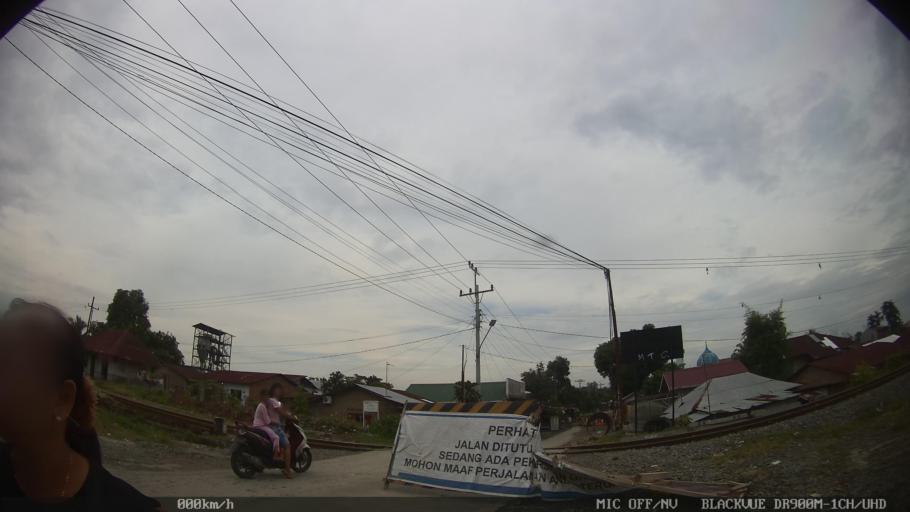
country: ID
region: North Sumatra
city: Sunggal
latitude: 3.6045
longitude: 98.6044
